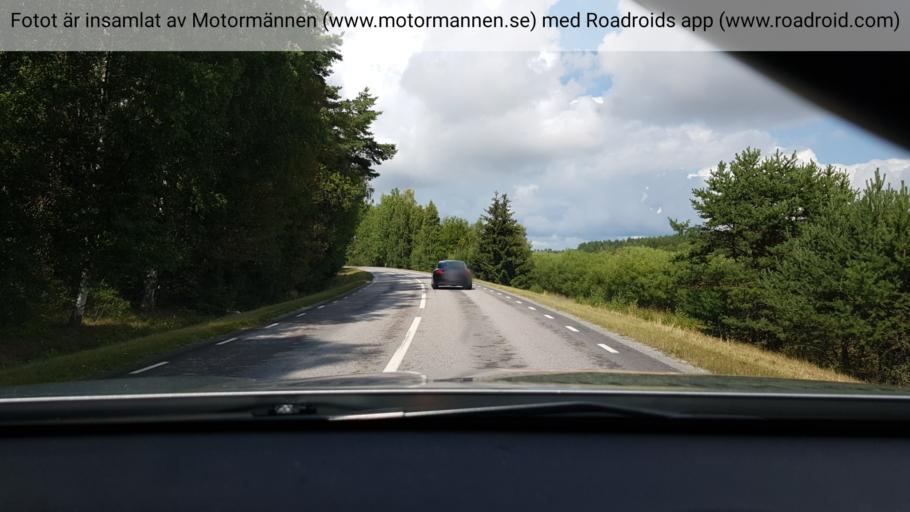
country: SE
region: Stockholm
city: Stenhamra
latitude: 59.3545
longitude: 17.6245
